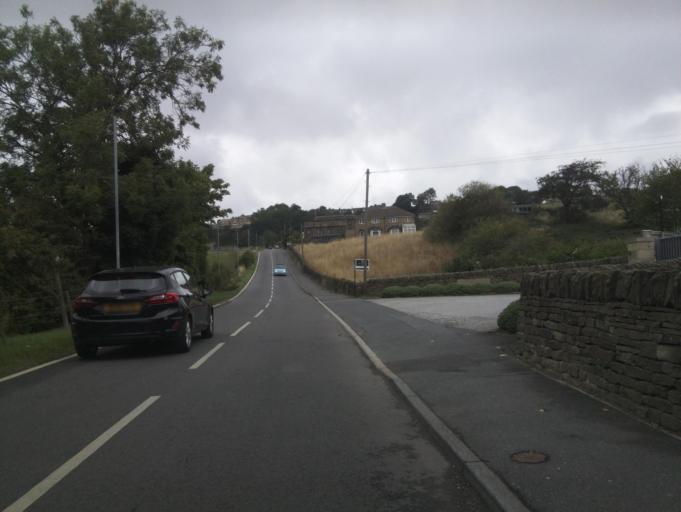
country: GB
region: England
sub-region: Kirklees
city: Shelley
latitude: 53.5931
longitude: -1.6895
